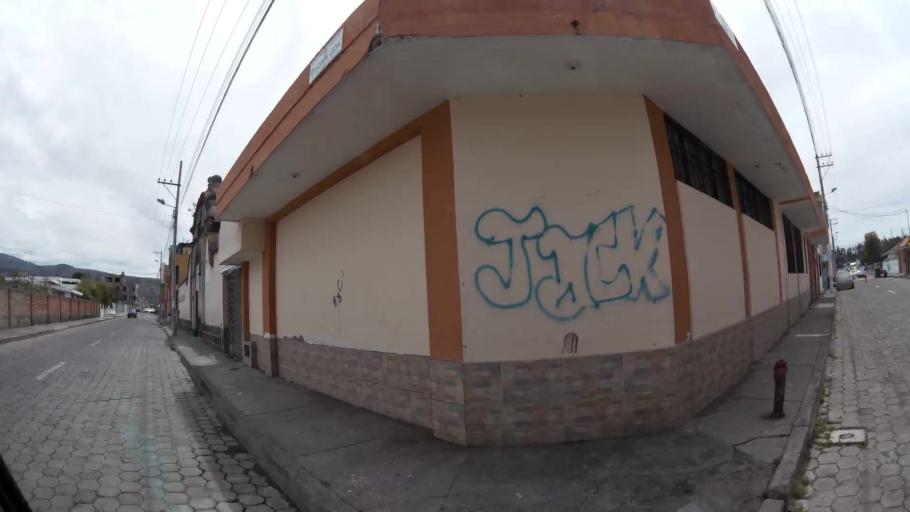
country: EC
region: Cotopaxi
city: San Miguel de Salcedo
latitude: -1.0427
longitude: -78.5935
